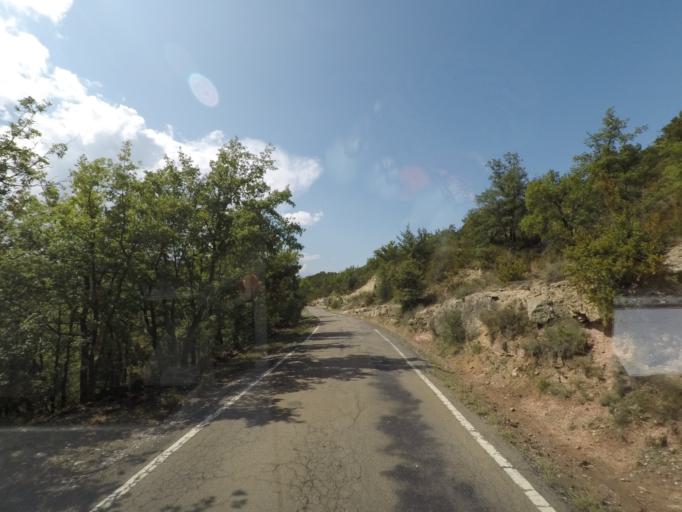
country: ES
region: Aragon
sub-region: Provincia de Huesca
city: Yebra de Basa
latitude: 42.3982
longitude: -0.3407
